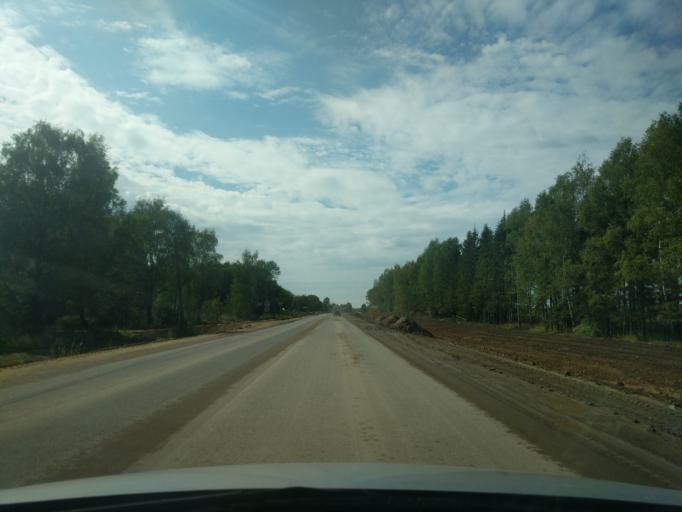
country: RU
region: Kostroma
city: Sudislavl'
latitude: 57.8734
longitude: 41.6651
